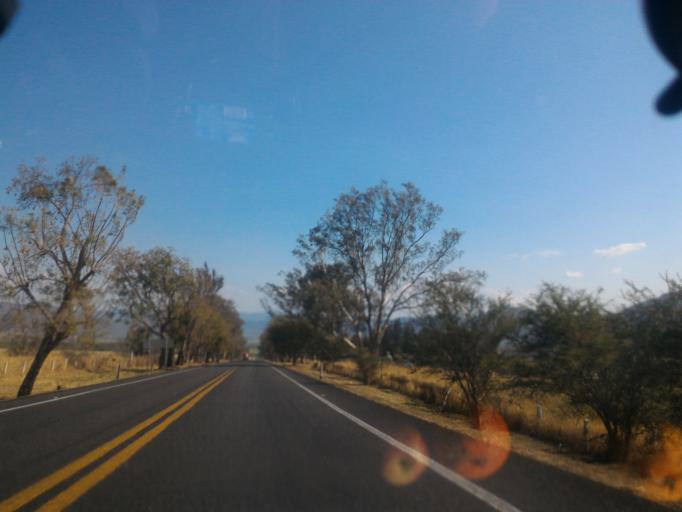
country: MX
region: Jalisco
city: Tuxpan
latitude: 19.5445
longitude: -103.4290
